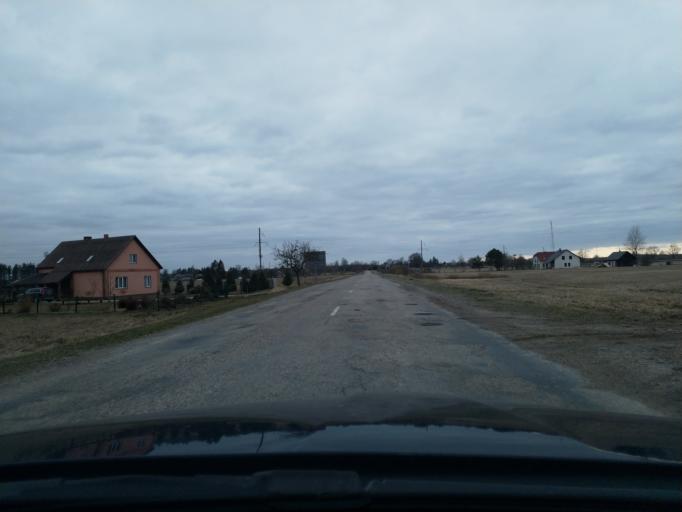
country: LV
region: Kuldigas Rajons
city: Kuldiga
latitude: 56.9721
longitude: 22.0096
